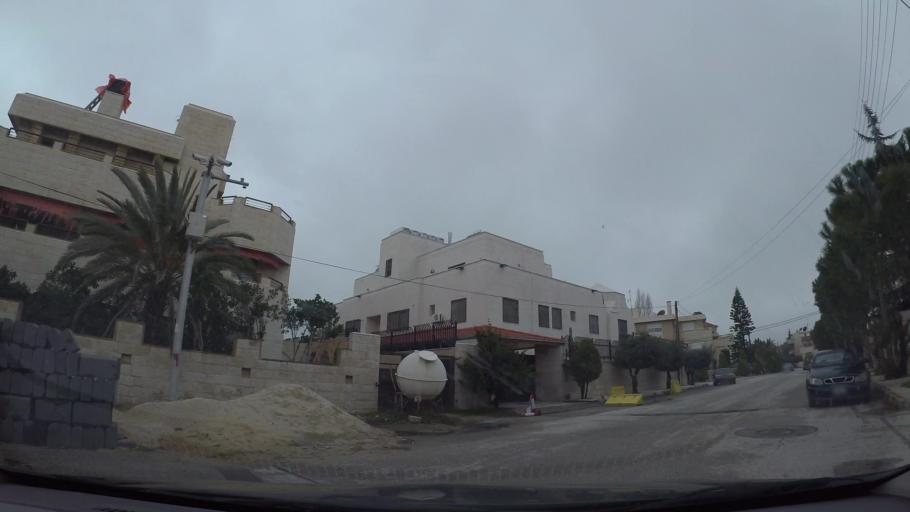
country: JO
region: Amman
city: Al Bunayyat ash Shamaliyah
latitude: 31.9449
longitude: 35.8776
